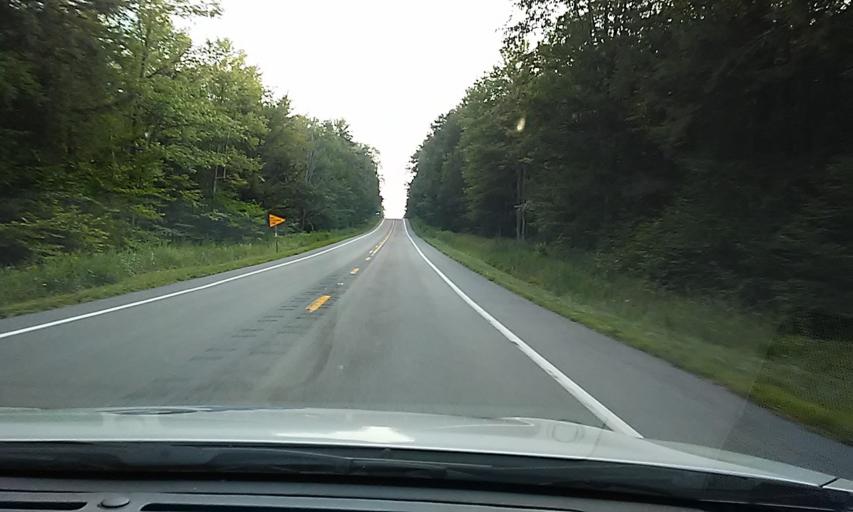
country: US
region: Pennsylvania
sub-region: Warren County
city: Sheffield
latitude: 41.5623
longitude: -78.9894
